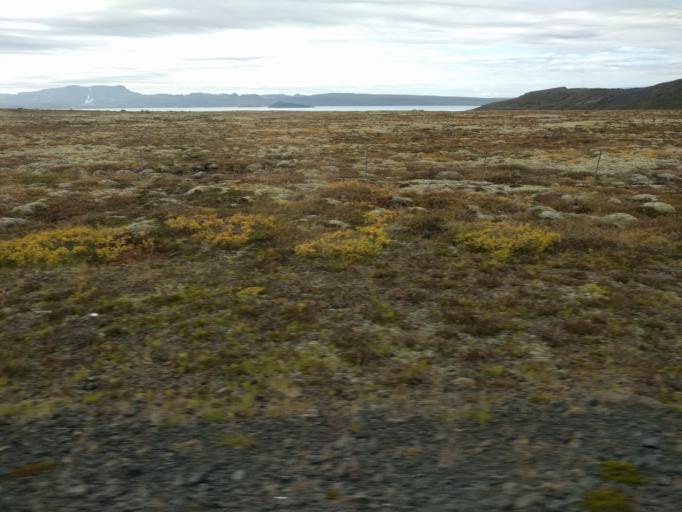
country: IS
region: South
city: Hveragerdi
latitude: 64.2124
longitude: -21.0469
